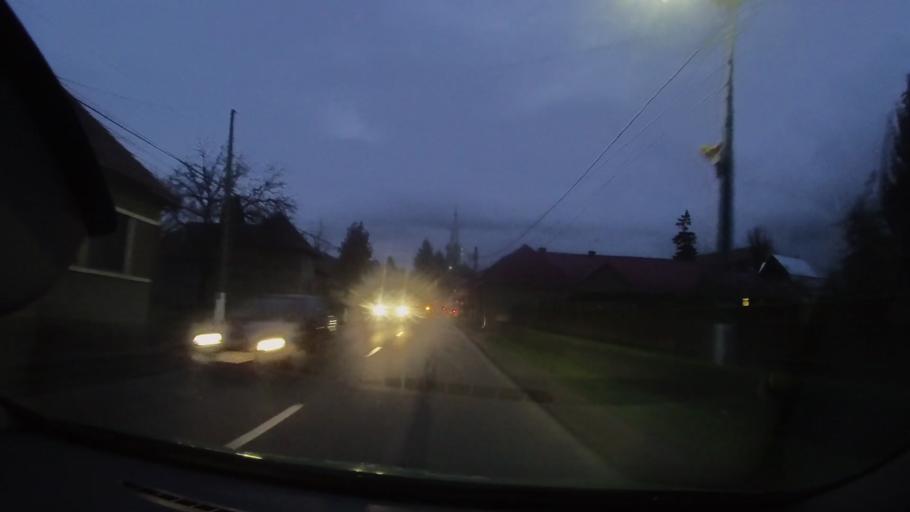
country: RO
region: Mures
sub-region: Comuna Gurghiu
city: Gurghiu
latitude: 46.7728
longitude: 24.8546
